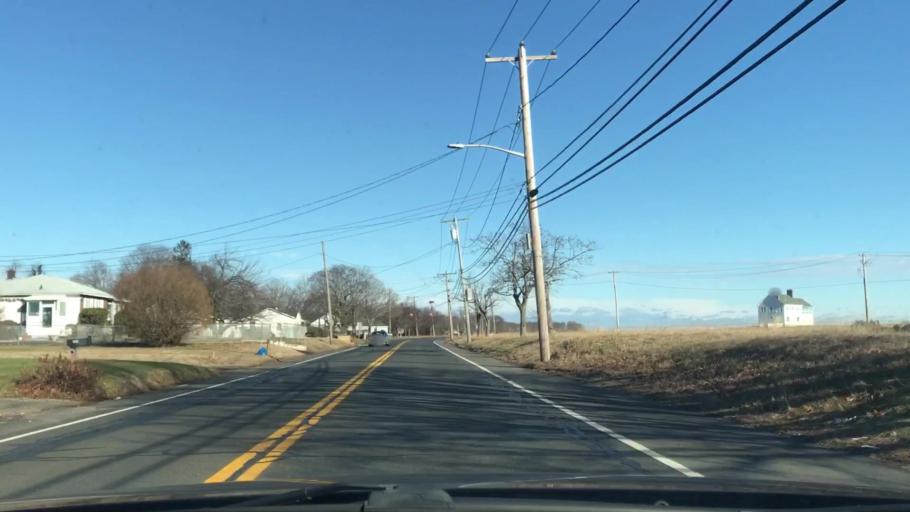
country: US
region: New York
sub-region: Suffolk County
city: Riverhead
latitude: 40.9446
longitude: -72.6564
